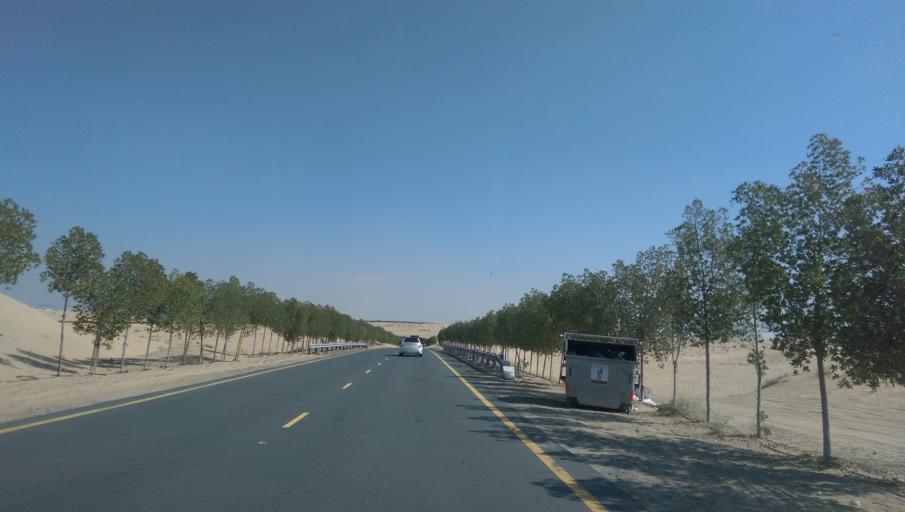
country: AE
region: Dubai
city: Dubai
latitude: 24.9835
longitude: 55.3438
